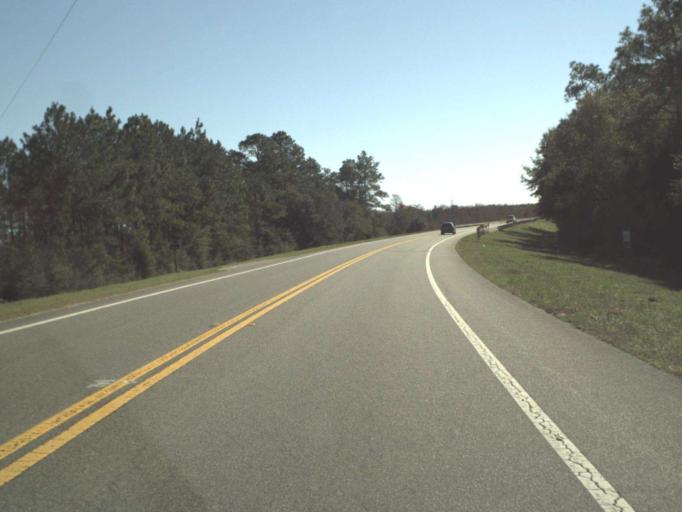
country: US
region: Florida
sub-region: Santa Rosa County
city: East Milton
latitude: 30.5838
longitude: -86.9303
